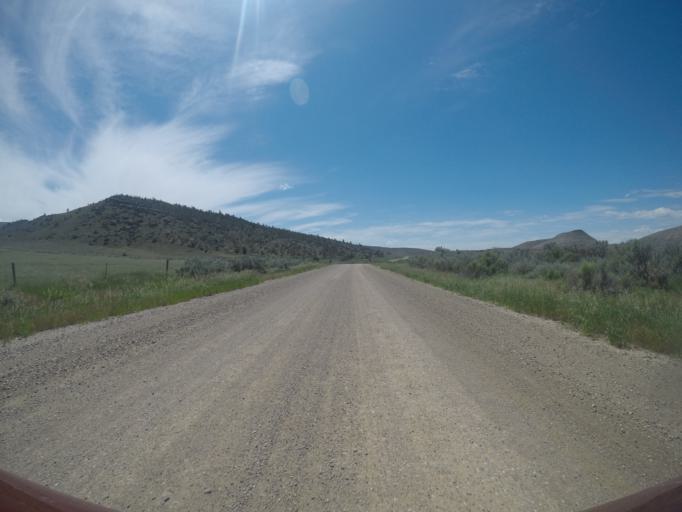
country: US
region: Montana
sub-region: Carbon County
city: Red Lodge
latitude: 45.2244
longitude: -108.8419
